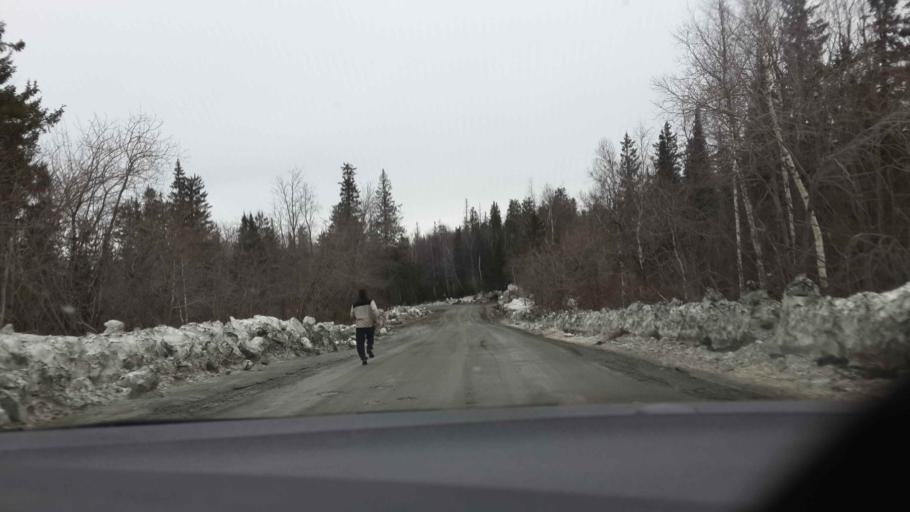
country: RU
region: Chelyabinsk
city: Magnitka
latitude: 55.2723
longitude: 59.6990
